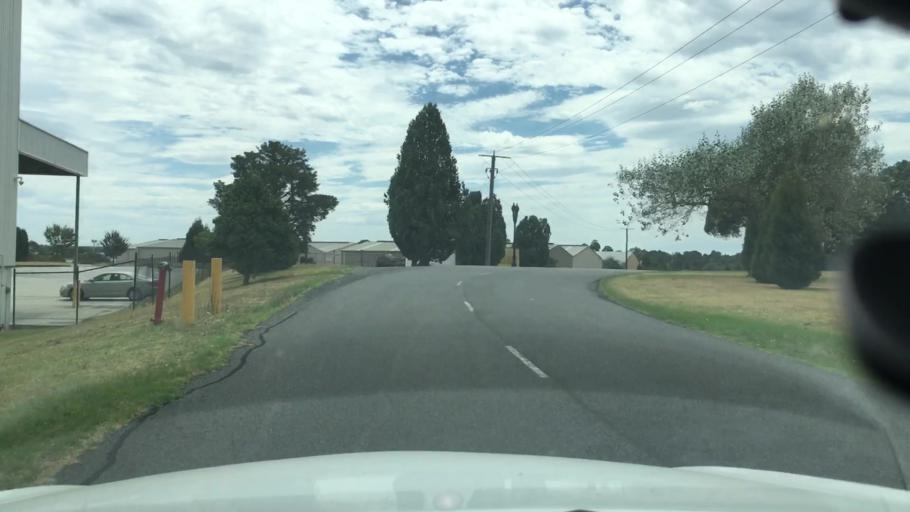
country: AU
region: Victoria
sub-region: Knox
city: Scoresby
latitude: -37.9027
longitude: 145.2254
